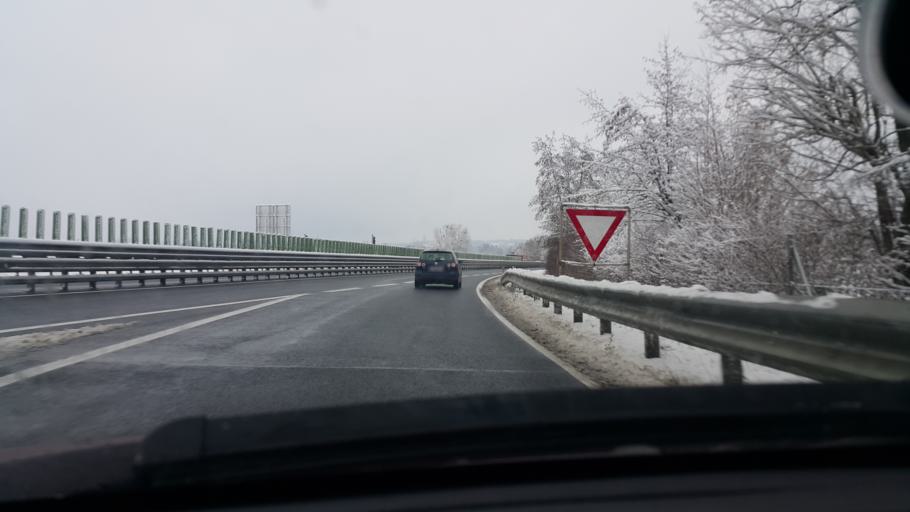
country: AT
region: Styria
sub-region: Politischer Bezirk Voitsberg
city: Mooskirchen
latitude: 46.9815
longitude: 15.2725
